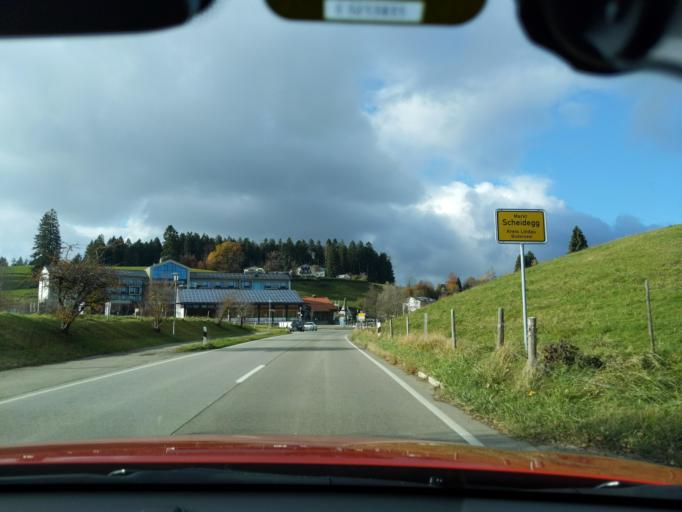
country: DE
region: Bavaria
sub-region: Swabia
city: Scheidegg
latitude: 47.5728
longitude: 9.8467
